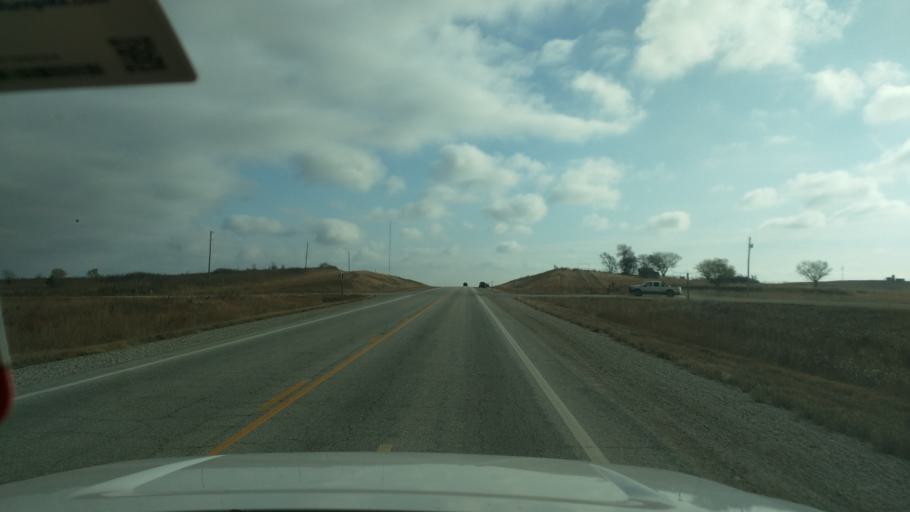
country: US
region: Kansas
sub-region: Chautauqua County
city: Sedan
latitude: 37.0834
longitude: -96.1997
